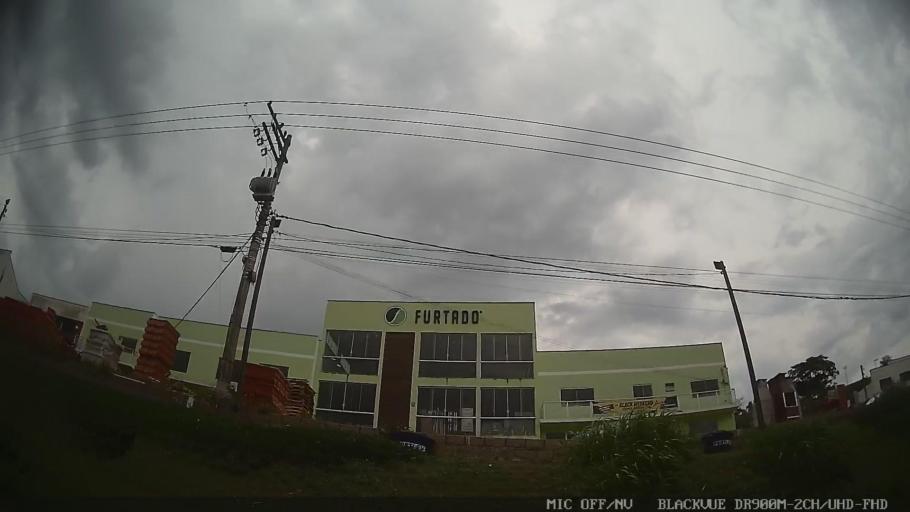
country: BR
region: Sao Paulo
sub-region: Amparo
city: Amparo
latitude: -22.7213
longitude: -46.7920
